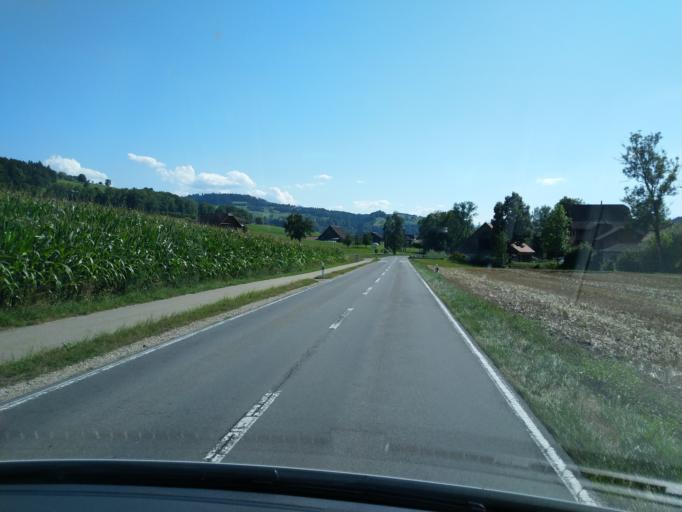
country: CH
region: Lucerne
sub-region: Entlebuch District
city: Werthenstein
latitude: 47.0729
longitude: 8.1058
